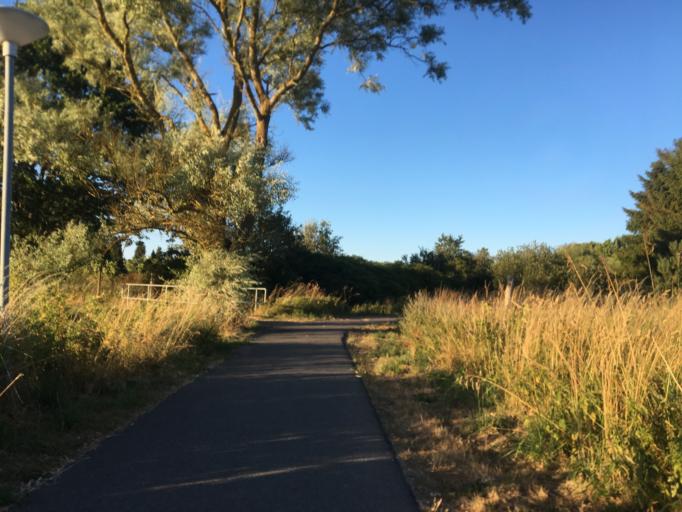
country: DK
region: Central Jutland
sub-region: Syddjurs Kommune
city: Hornslet
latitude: 56.3164
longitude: 10.3263
